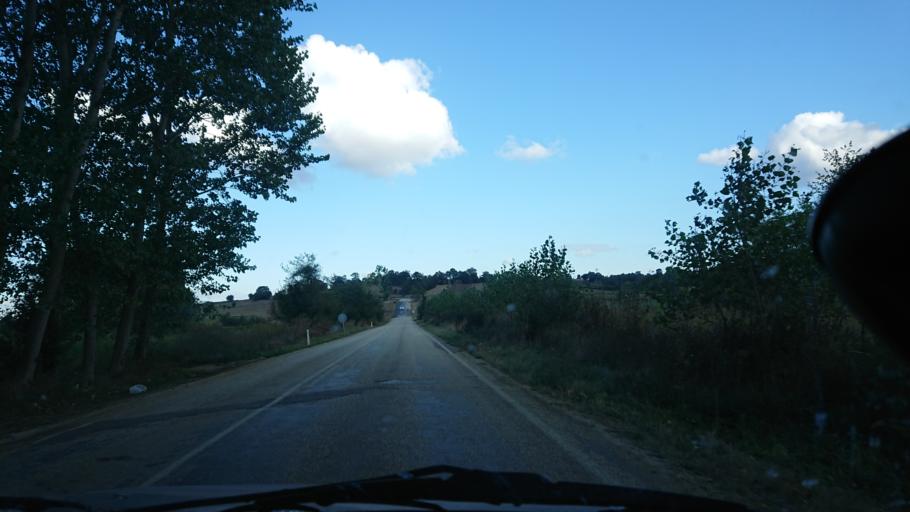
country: TR
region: Bilecik
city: Pazaryeri
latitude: 40.0095
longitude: 29.8627
